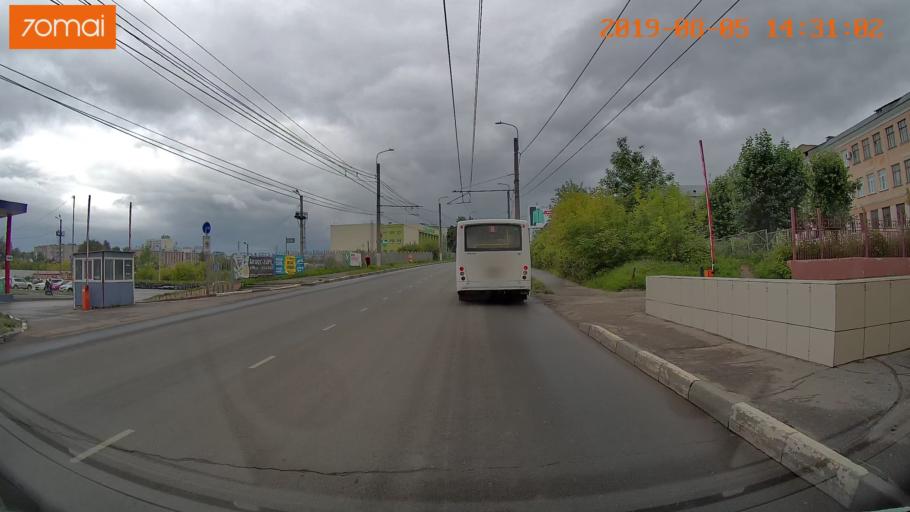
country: RU
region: Ivanovo
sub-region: Gorod Ivanovo
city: Ivanovo
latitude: 56.9854
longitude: 41.0064
